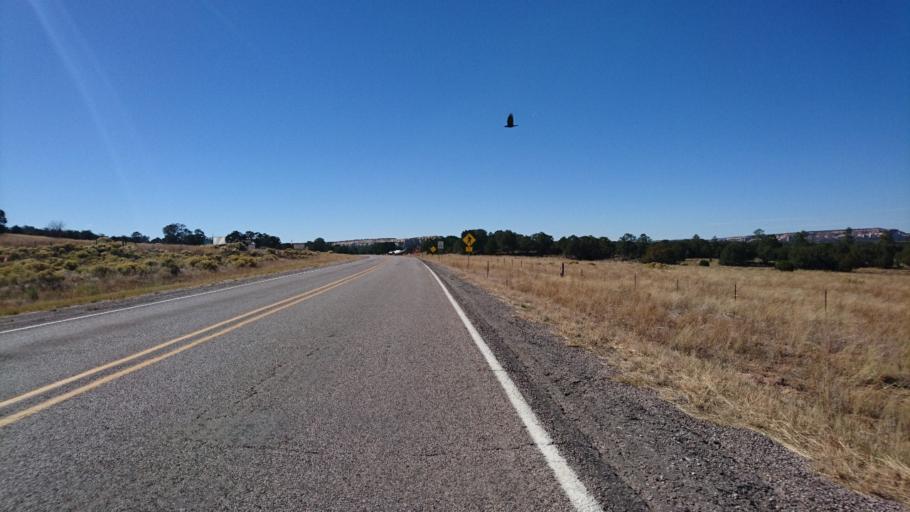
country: US
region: New Mexico
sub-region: McKinley County
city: Thoreau
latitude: 35.0451
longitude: -108.3165
